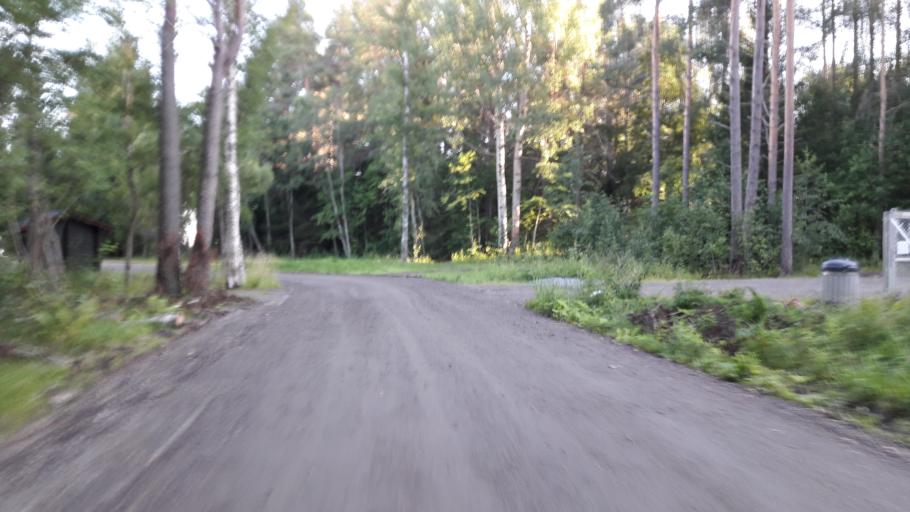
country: FI
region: North Karelia
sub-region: Joensuu
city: Joensuu
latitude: 62.6136
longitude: 29.6951
